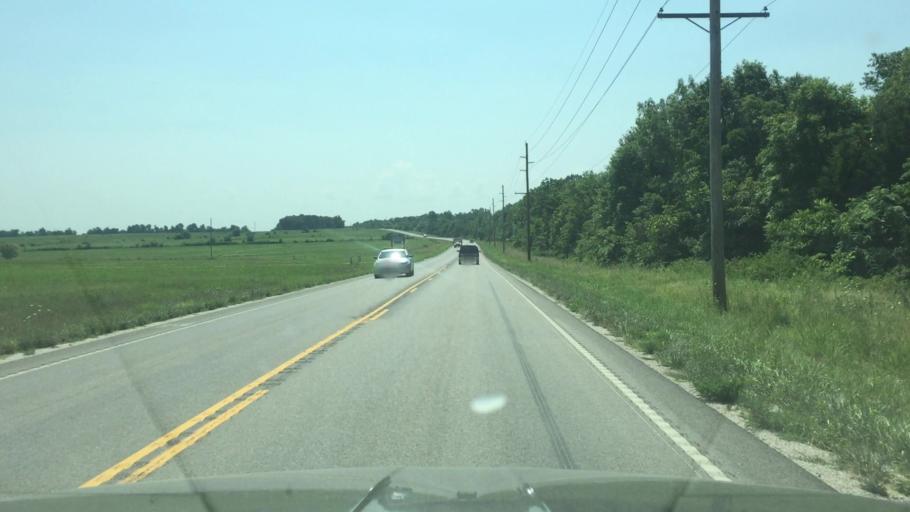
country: US
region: Missouri
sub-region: Miller County
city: Eldon
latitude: 38.3920
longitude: -92.7093
